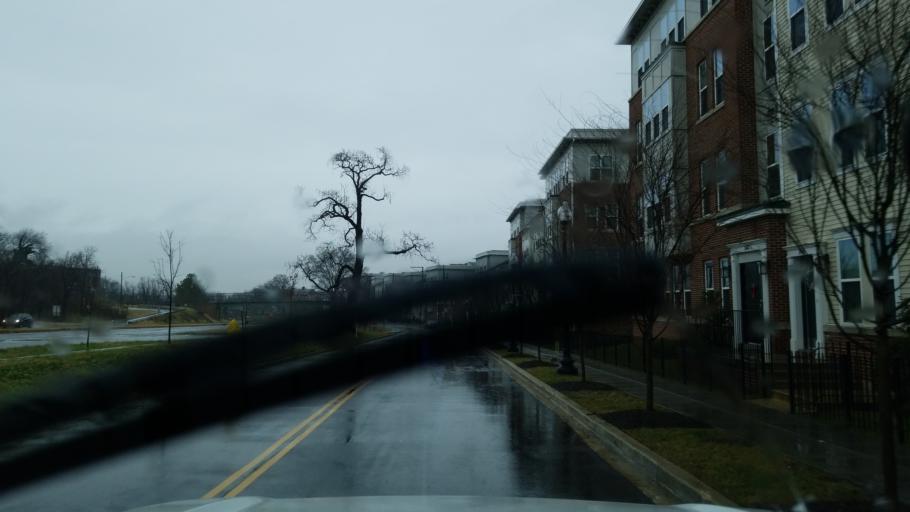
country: US
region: Maryland
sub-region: Prince George's County
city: Glassmanor
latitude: 38.8570
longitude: -76.9934
